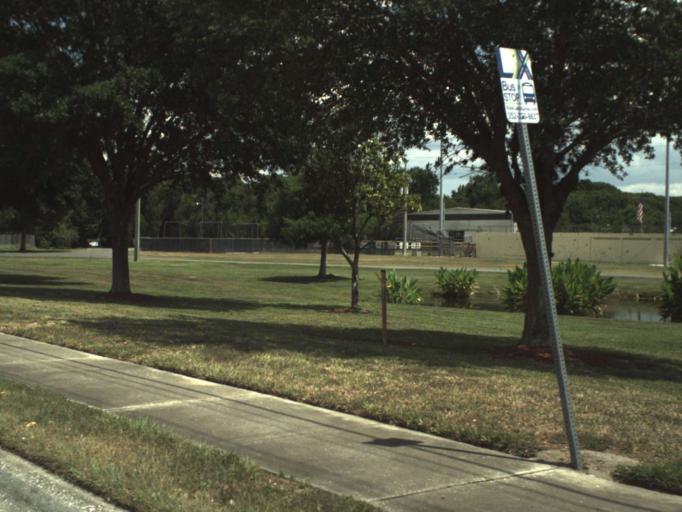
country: US
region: Florida
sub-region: Lake County
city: Leesburg
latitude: 28.8066
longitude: -81.8731
